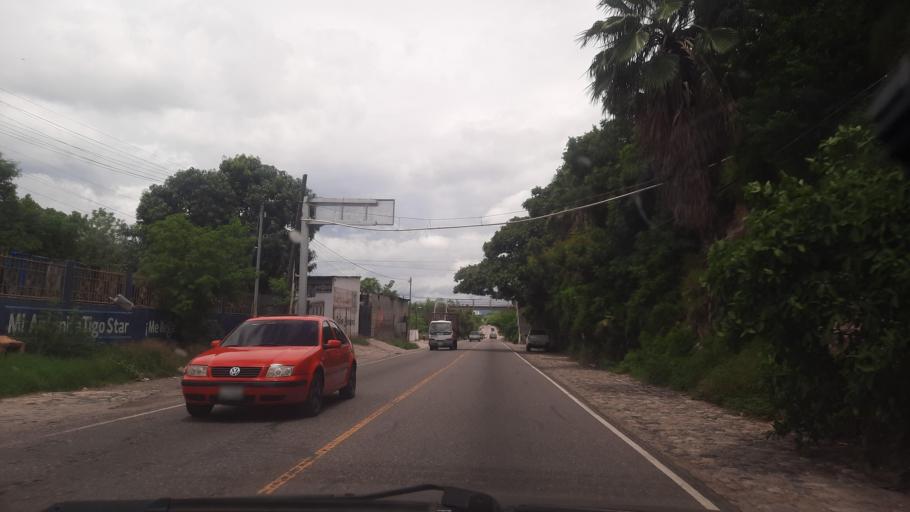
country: GT
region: Zacapa
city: Estanzuela
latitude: 15.0016
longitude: -89.5699
